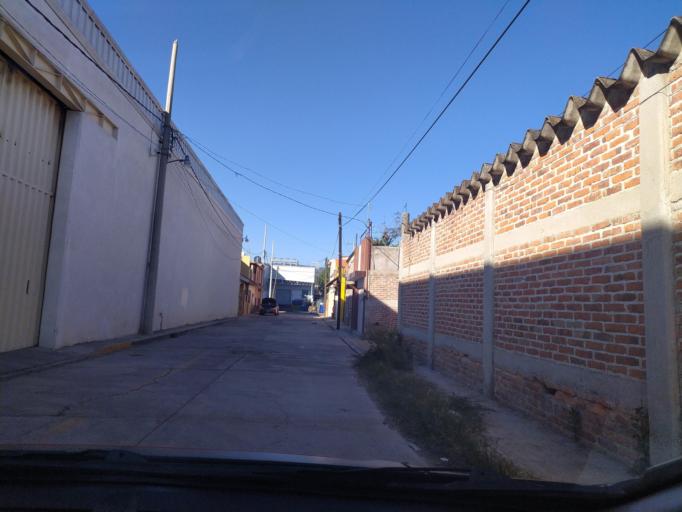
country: MX
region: Guanajuato
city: Ciudad Manuel Doblado
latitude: 20.7256
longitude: -101.9466
